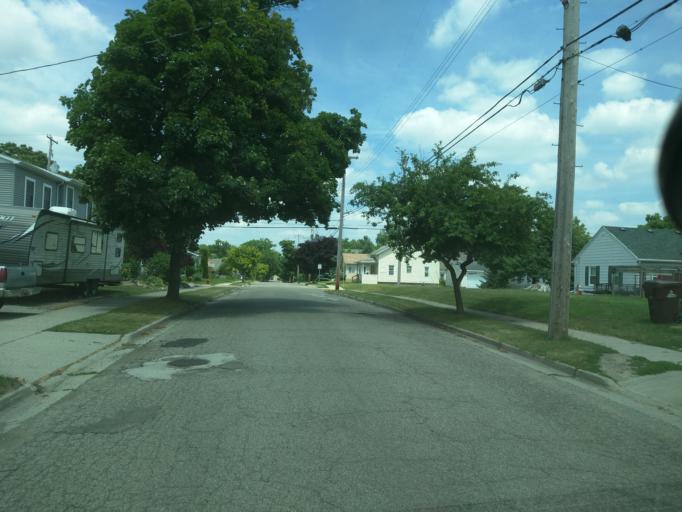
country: US
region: Michigan
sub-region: Ingham County
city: Lansing
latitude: 42.7595
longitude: -84.5518
